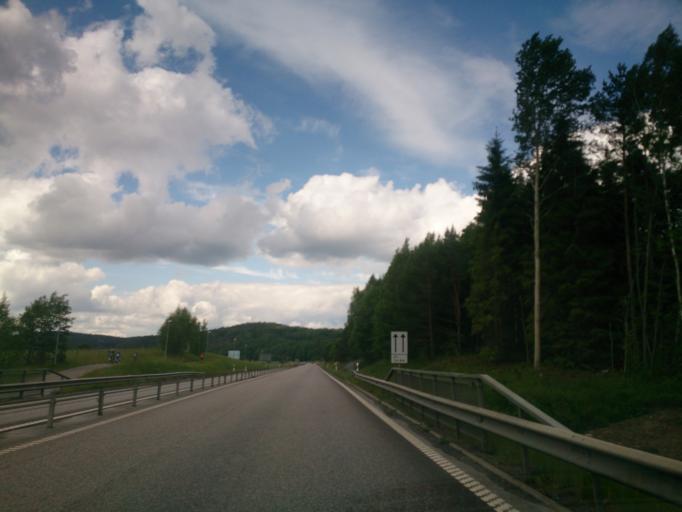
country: SE
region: OEstergoetland
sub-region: Norrkopings Kommun
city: Jursla
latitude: 58.6603
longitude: 16.1691
